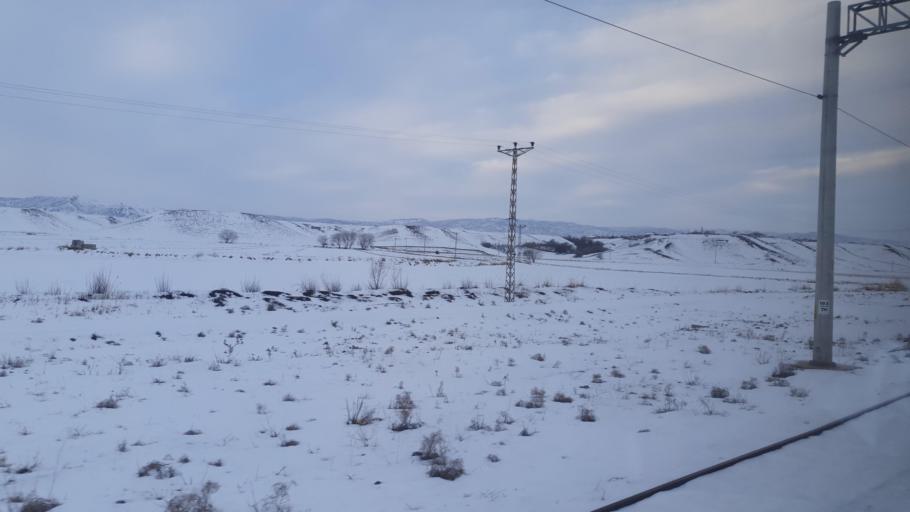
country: TR
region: Kirsehir
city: Mecidiye
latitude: 39.6861
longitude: 34.3998
